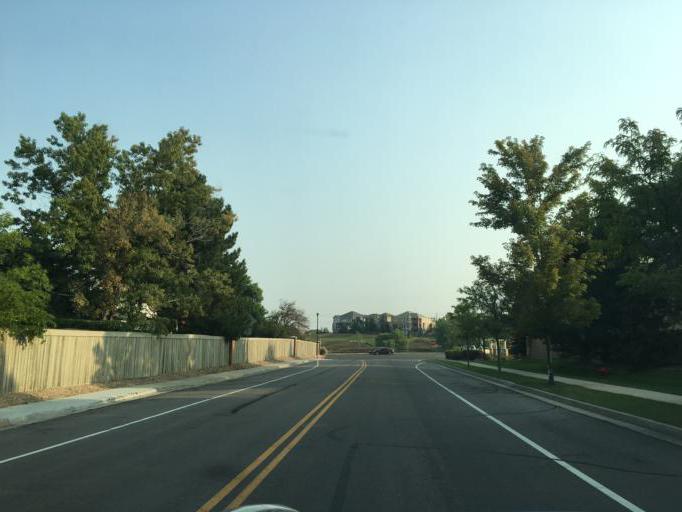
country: US
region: Colorado
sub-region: Adams County
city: Westminster
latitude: 39.8840
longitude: -105.0486
